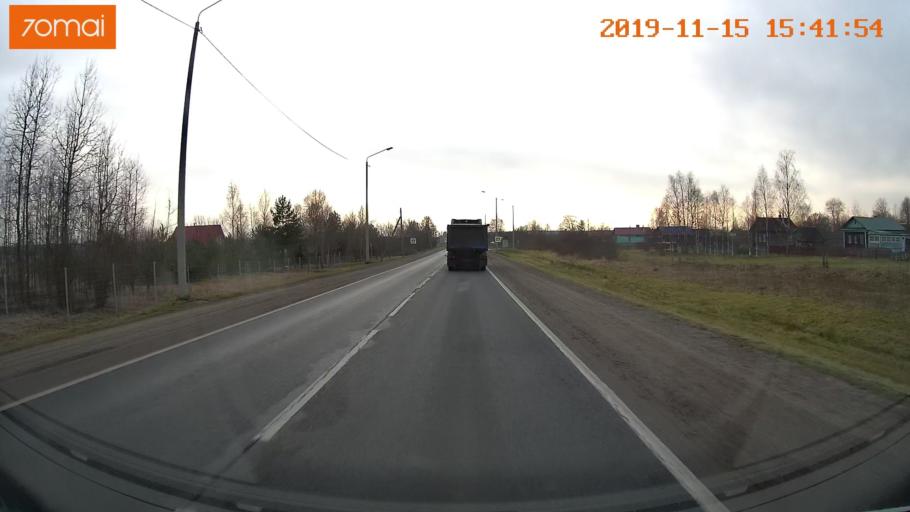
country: RU
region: Jaroslavl
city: Danilov
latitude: 57.9966
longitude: 40.0434
